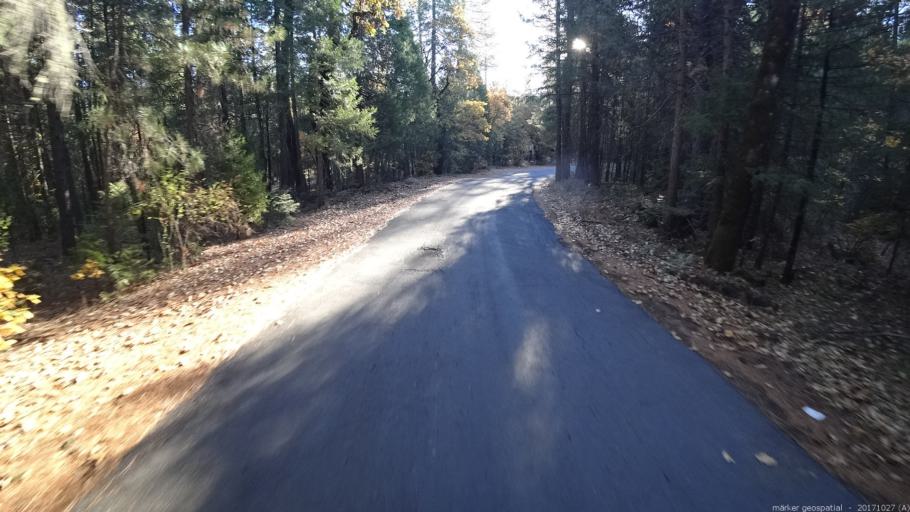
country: US
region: California
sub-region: Shasta County
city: Burney
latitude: 41.0108
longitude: -121.8972
